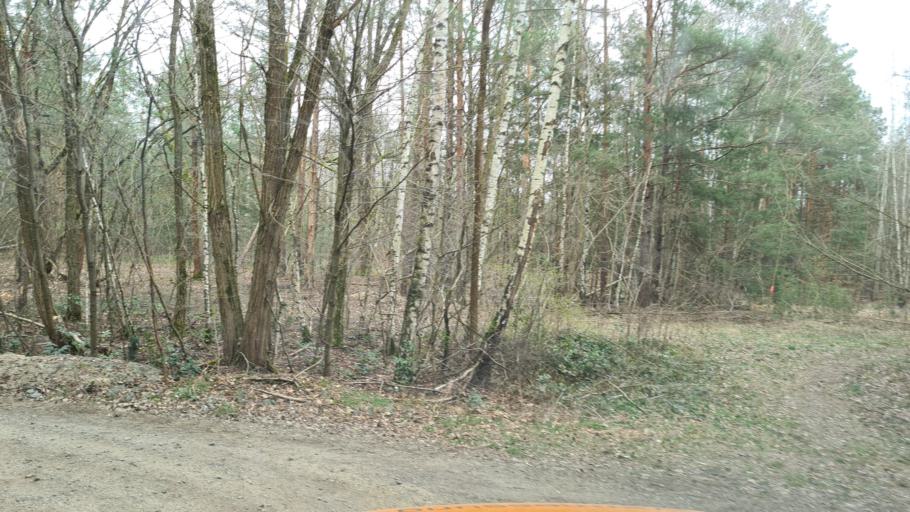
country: DE
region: Brandenburg
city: Lauchhammer
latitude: 51.5105
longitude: 13.7250
